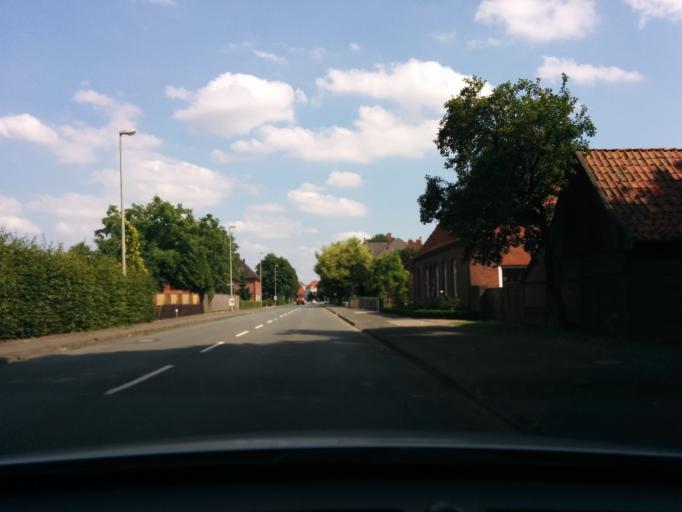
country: DE
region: North Rhine-Westphalia
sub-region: Regierungsbezirk Munster
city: Ochtrup
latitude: 52.1989
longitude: 7.2318
